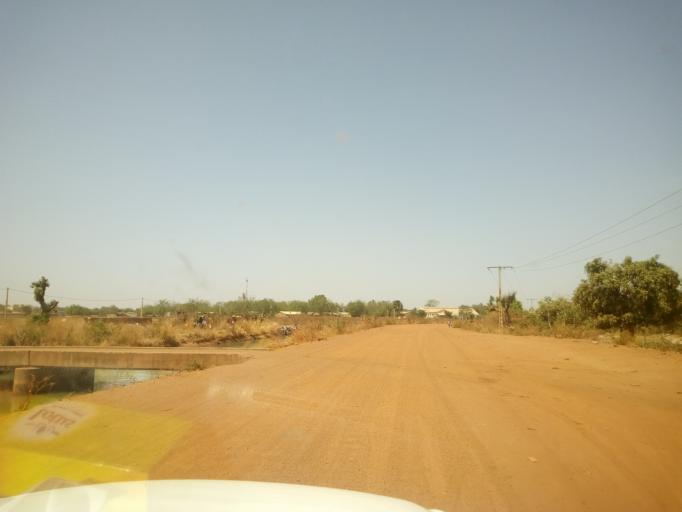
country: ML
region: Bamako
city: Bamako
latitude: 12.6199
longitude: -7.7731
